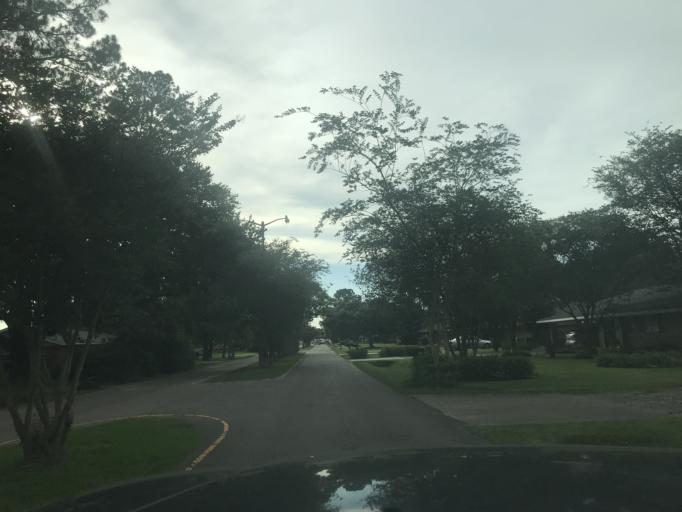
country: US
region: Louisiana
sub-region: Lafayette Parish
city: Lafayette
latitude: 30.1945
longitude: -92.0547
